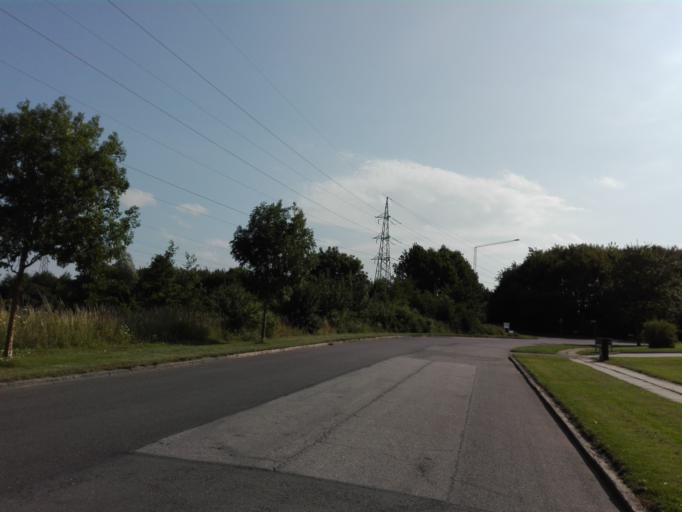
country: DK
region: Central Jutland
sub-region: Arhus Kommune
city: Trige
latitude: 56.2110
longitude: 10.1859
